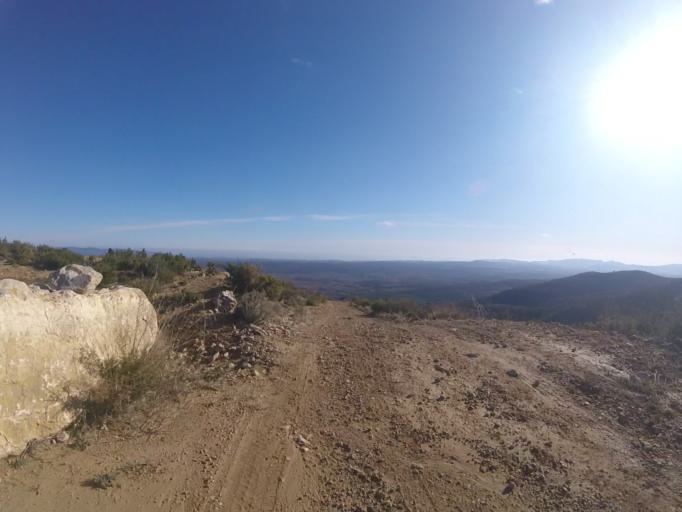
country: ES
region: Valencia
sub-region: Provincia de Castello
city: Sarratella
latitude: 40.3005
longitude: 0.0373
